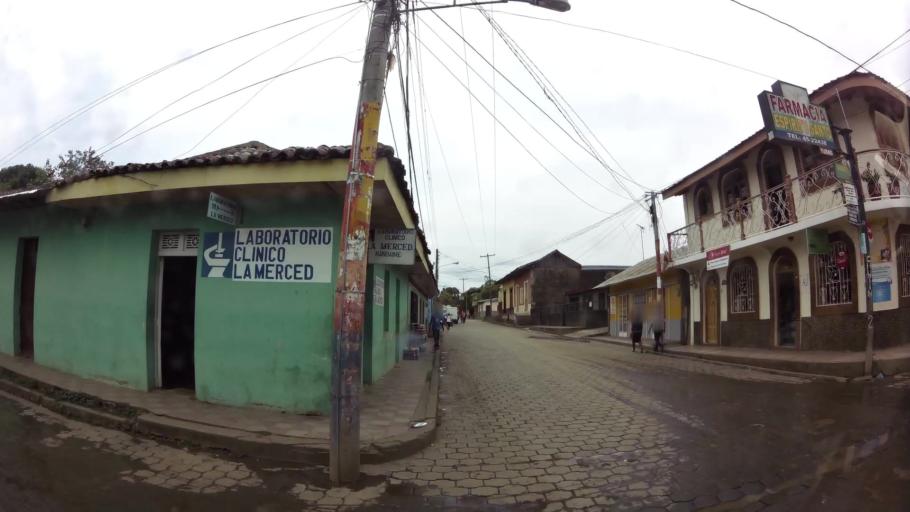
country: NI
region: Granada
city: Nandaime
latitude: 11.7565
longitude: -86.0552
